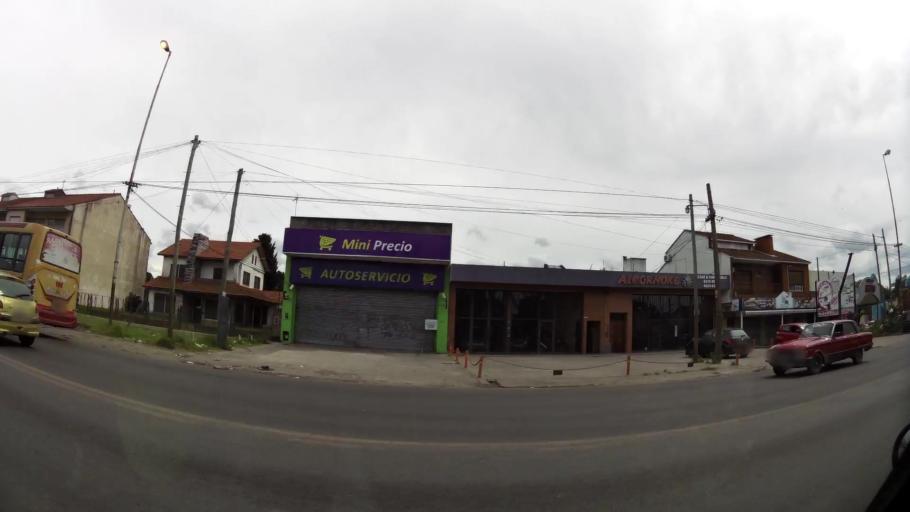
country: AR
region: Buenos Aires
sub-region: Partido de Quilmes
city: Quilmes
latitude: -34.7653
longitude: -58.2742
